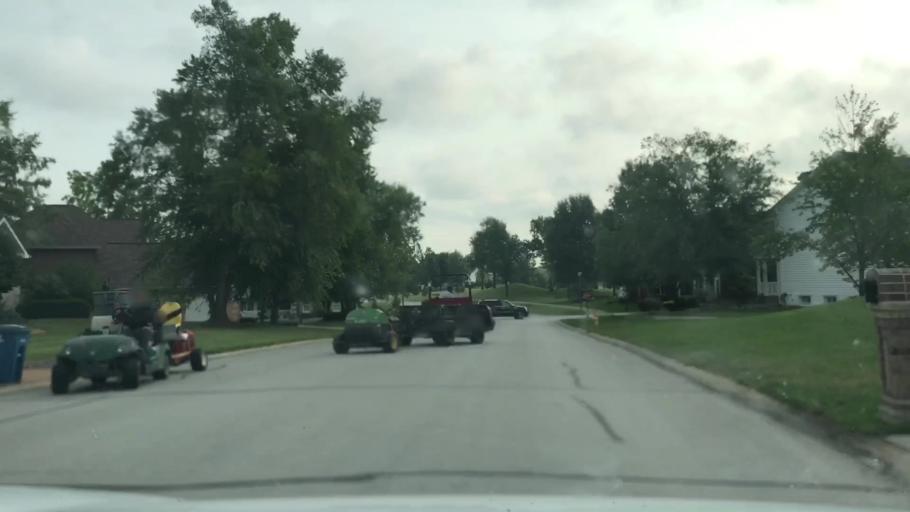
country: US
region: Missouri
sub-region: Saint Charles County
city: Cottleville
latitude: 38.7173
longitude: -90.6337
